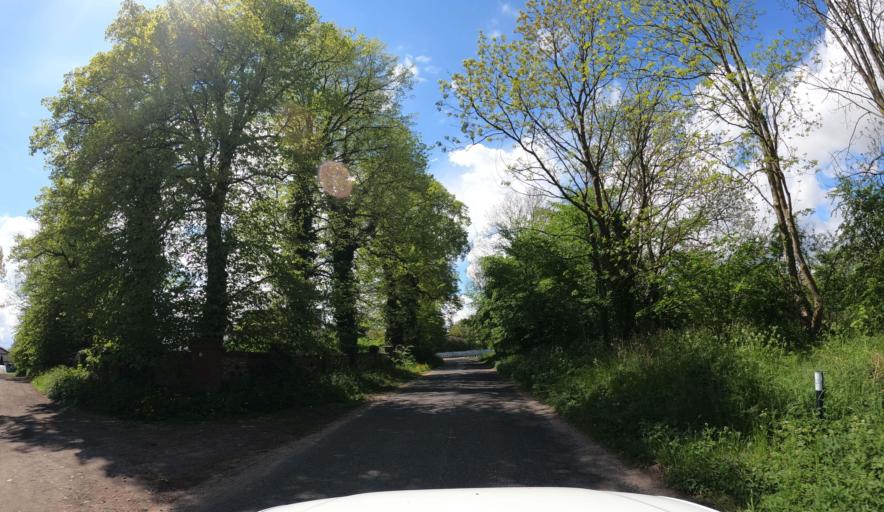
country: PL
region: West Pomeranian Voivodeship
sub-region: Powiat kamienski
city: Wolin
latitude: 53.9063
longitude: 14.6748
